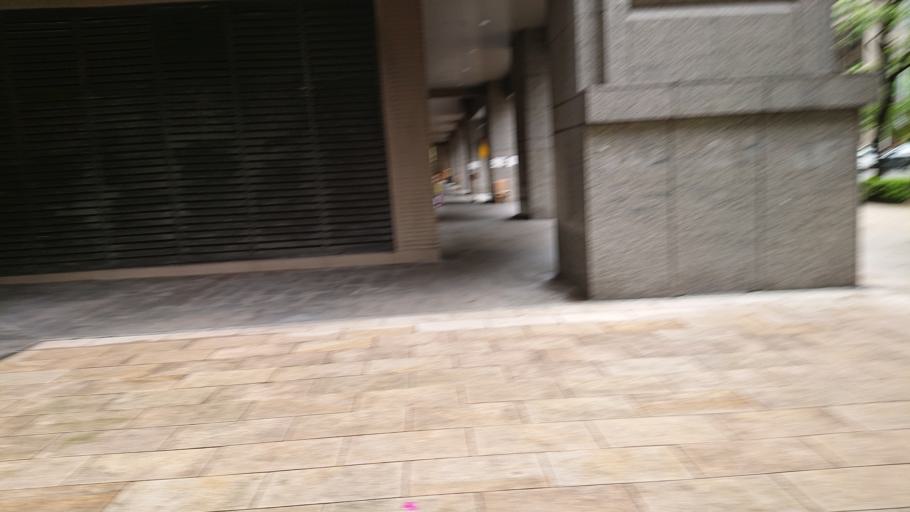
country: TW
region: Taiwan
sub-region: Taoyuan
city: Taoyuan
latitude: 24.9474
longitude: 121.3820
